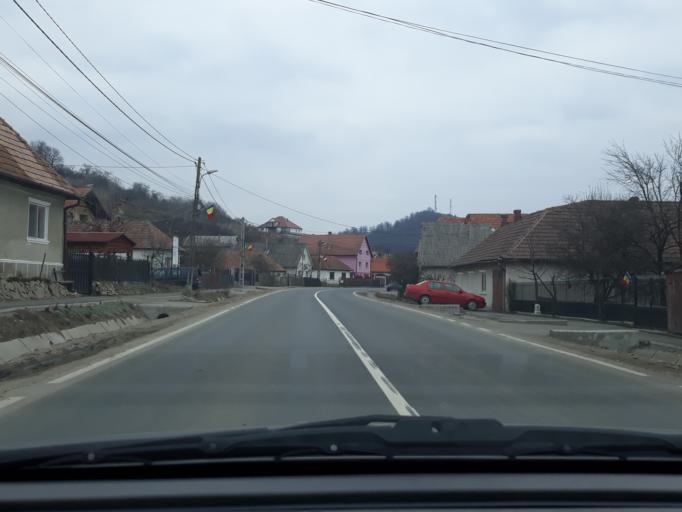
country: RO
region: Salaj
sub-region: Oras Simleu Silvaniei
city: Cehei
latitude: 47.2266
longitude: 22.7688
